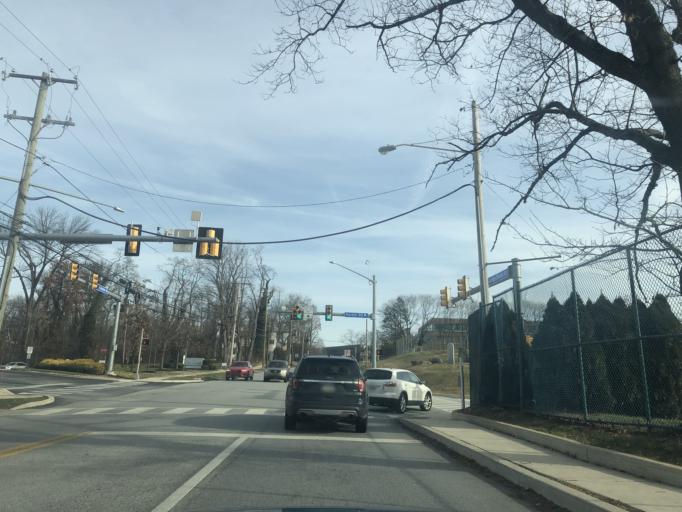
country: US
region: Pennsylvania
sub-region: Delaware County
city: Radnor
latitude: 40.0417
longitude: -75.3627
